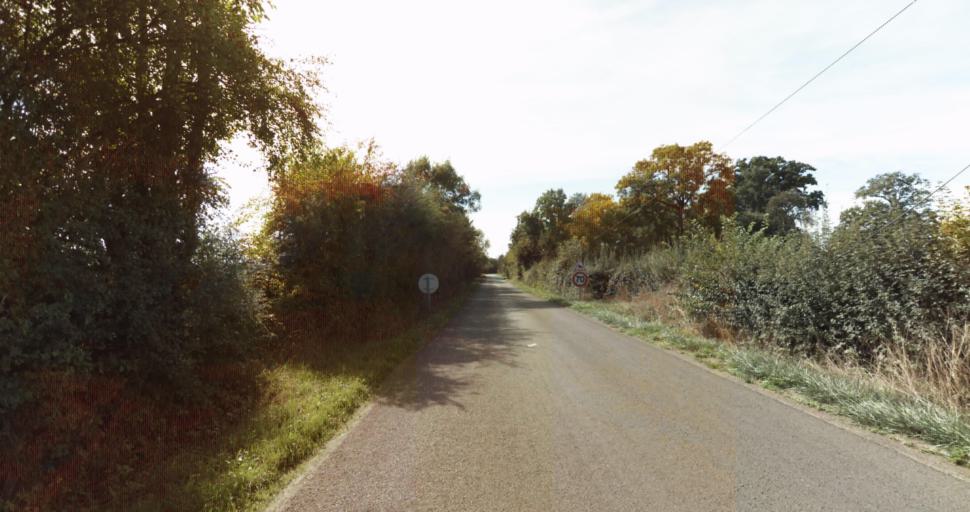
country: FR
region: Lower Normandy
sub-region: Departement de l'Orne
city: Sees
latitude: 48.7018
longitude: 0.2103
